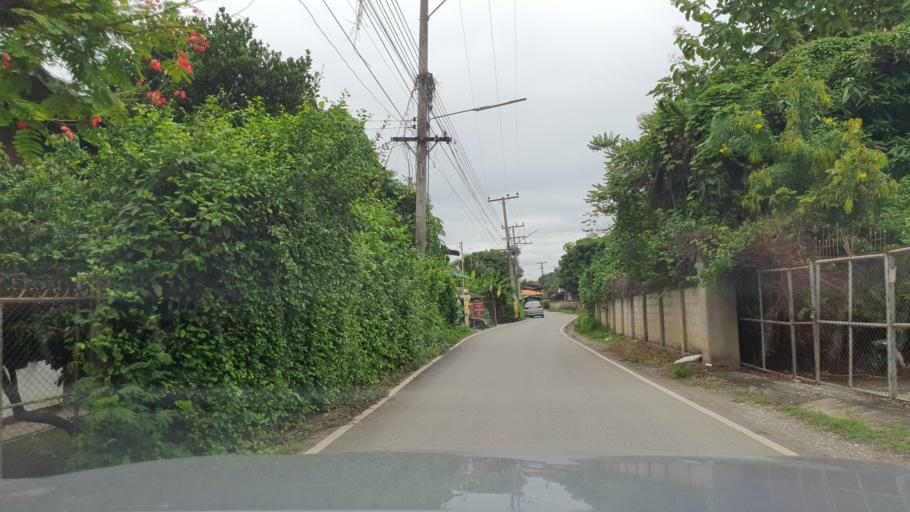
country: TH
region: Lamphun
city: Lamphun
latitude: 18.5961
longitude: 98.9729
